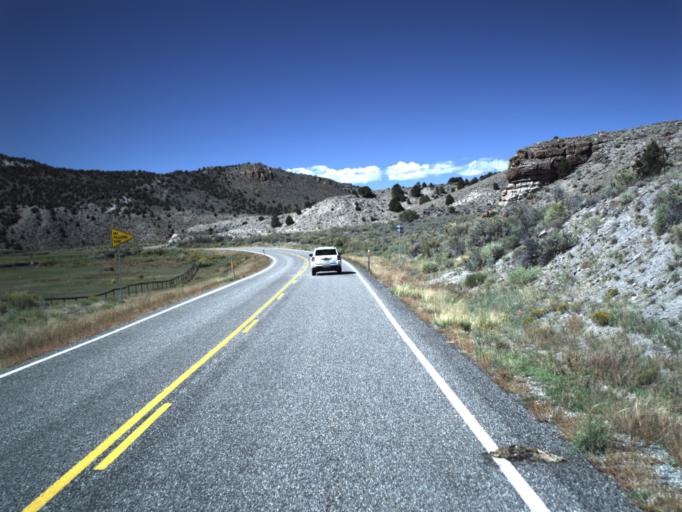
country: US
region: Utah
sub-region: Piute County
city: Junction
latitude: 38.1775
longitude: -112.0709
